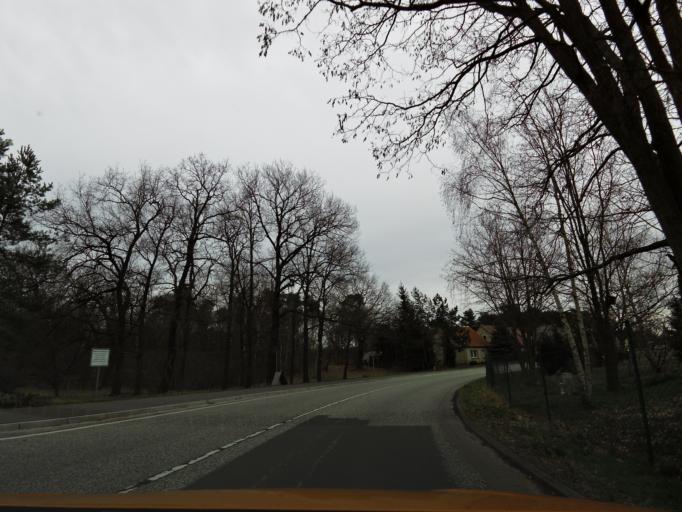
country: DE
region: Brandenburg
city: Bruck
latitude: 52.2070
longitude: 12.7874
